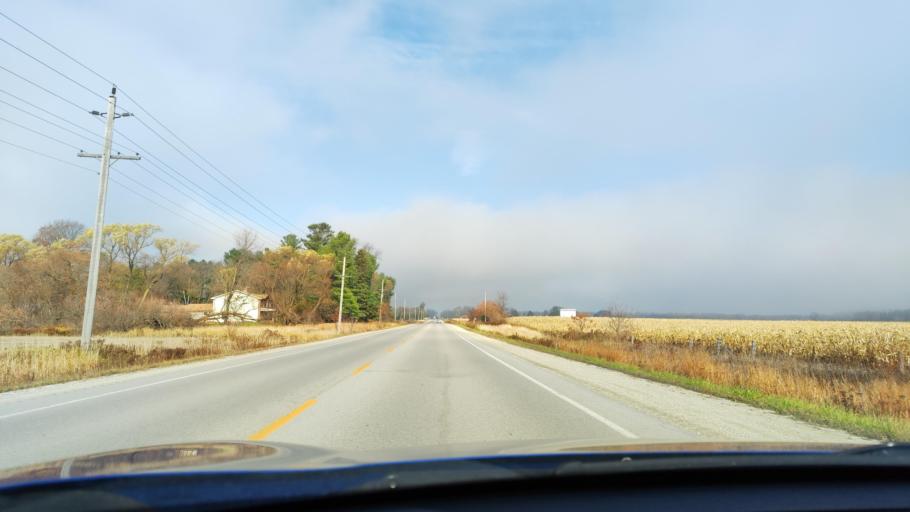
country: CA
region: Ontario
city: Wasaga Beach
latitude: 44.4488
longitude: -80.0696
